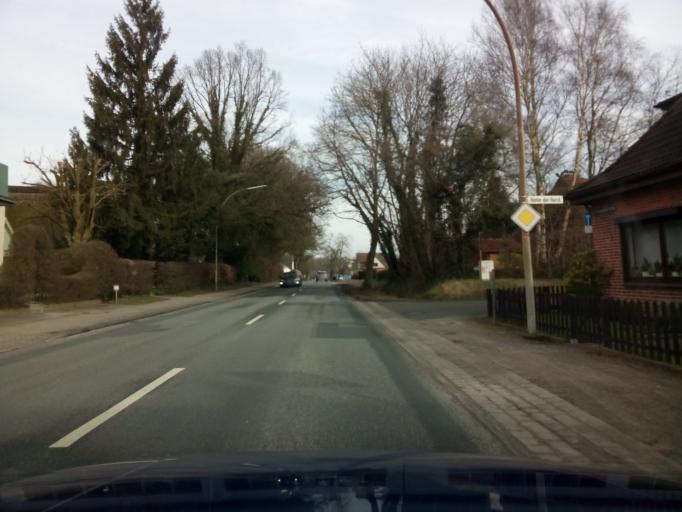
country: DE
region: Lower Saxony
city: Osterholz-Scharmbeck
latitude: 53.2391
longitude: 8.8129
